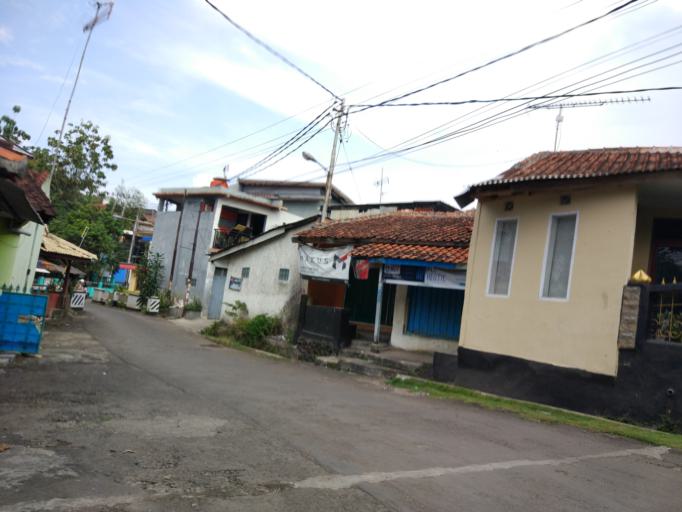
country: ID
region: West Java
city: Bandung
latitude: -6.9026
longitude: 107.6895
